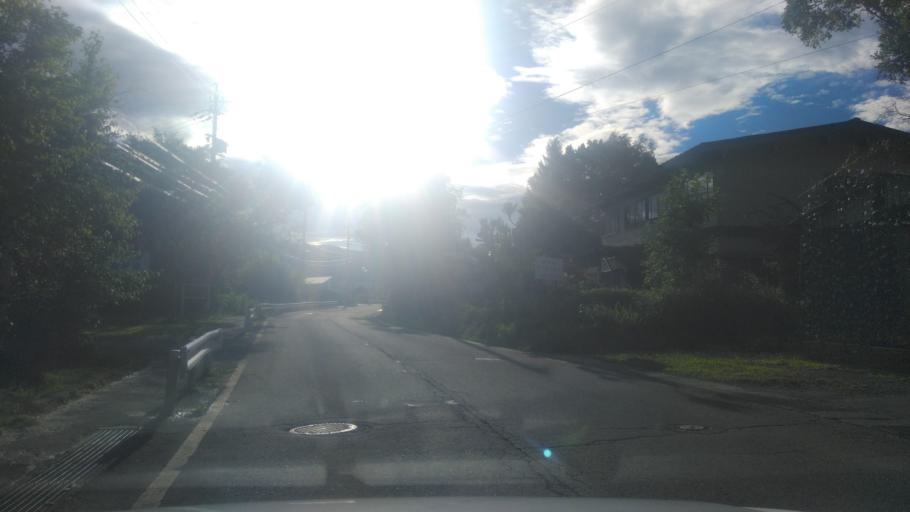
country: JP
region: Nagano
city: Suzaka
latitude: 36.5339
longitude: 138.3257
